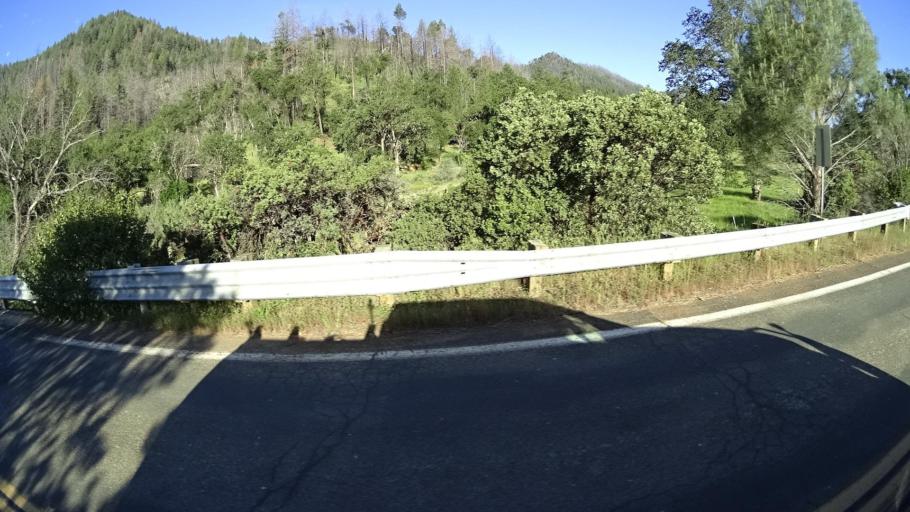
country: US
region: California
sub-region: Lake County
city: Upper Lake
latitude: 39.2507
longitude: -122.9527
